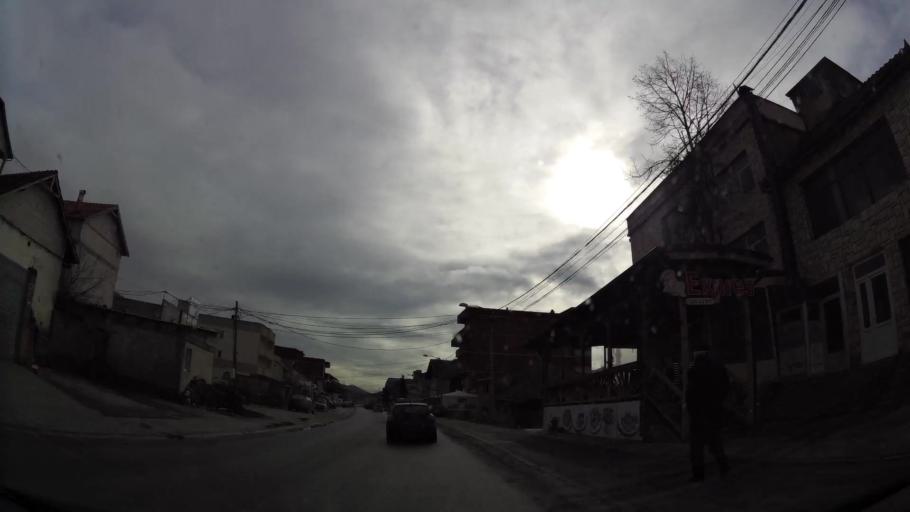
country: XK
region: Ferizaj
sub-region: Hani i Elezit
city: Hani i Elezit
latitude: 42.1520
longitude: 21.2972
